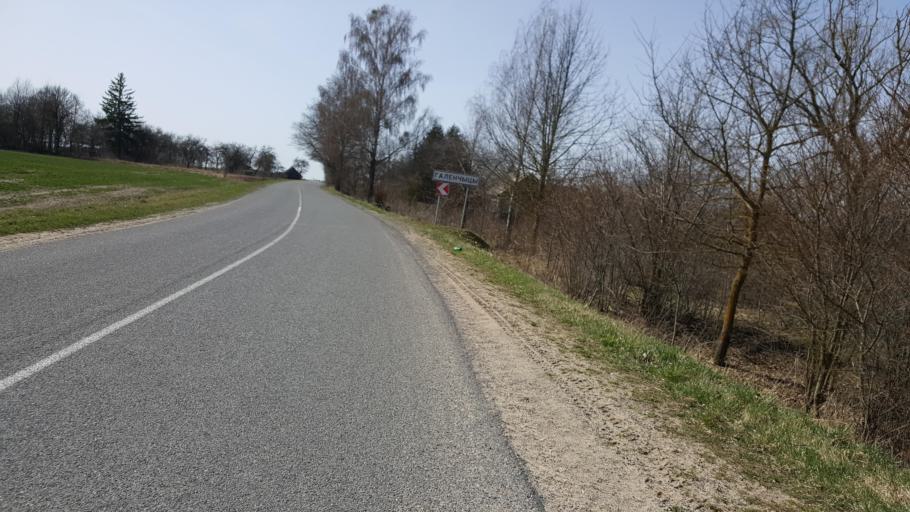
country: BY
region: Brest
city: Kamyanyets
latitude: 52.4643
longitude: 23.7260
